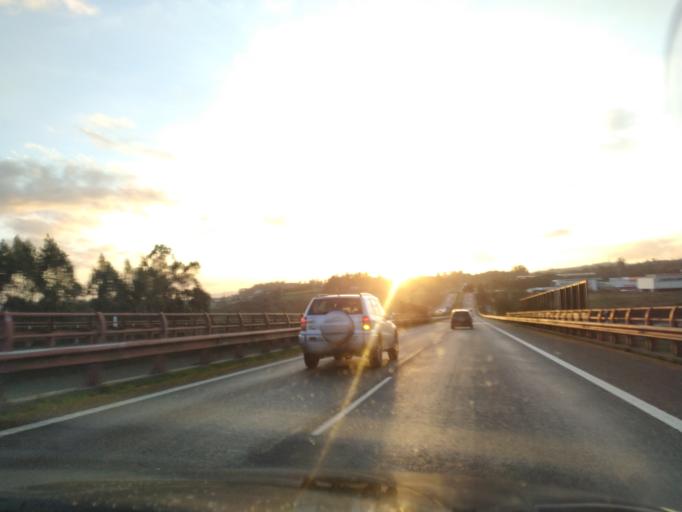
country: ES
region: Galicia
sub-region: Provincia da Coruna
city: Santiago de Compostela
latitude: 42.9006
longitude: -8.5012
